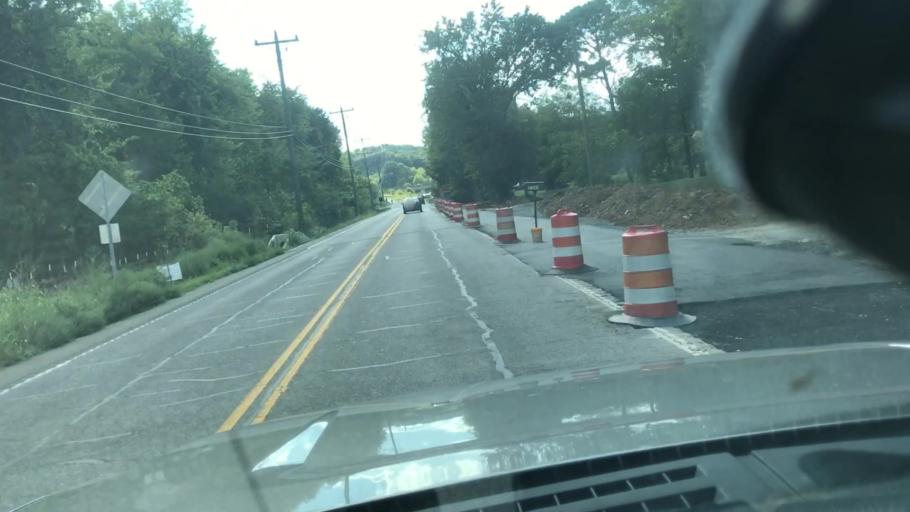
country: US
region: Tennessee
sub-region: Cheatham County
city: Pegram
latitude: 36.0353
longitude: -86.9691
